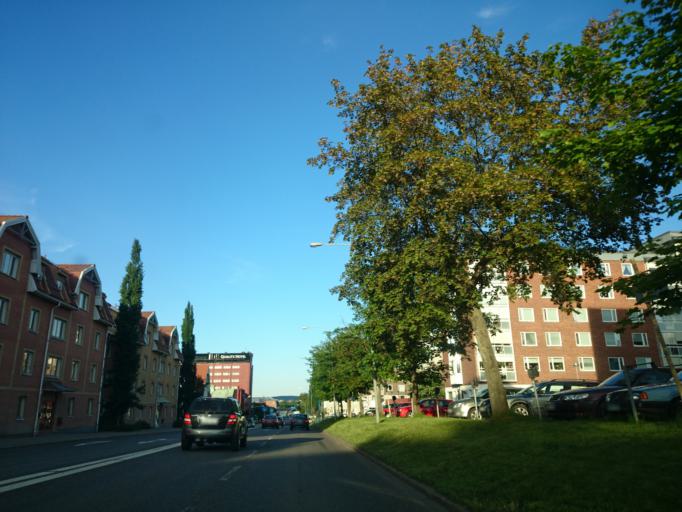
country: SE
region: Vaesternorrland
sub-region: Sundsvalls Kommun
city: Sundsvall
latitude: 62.3864
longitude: 17.3026
